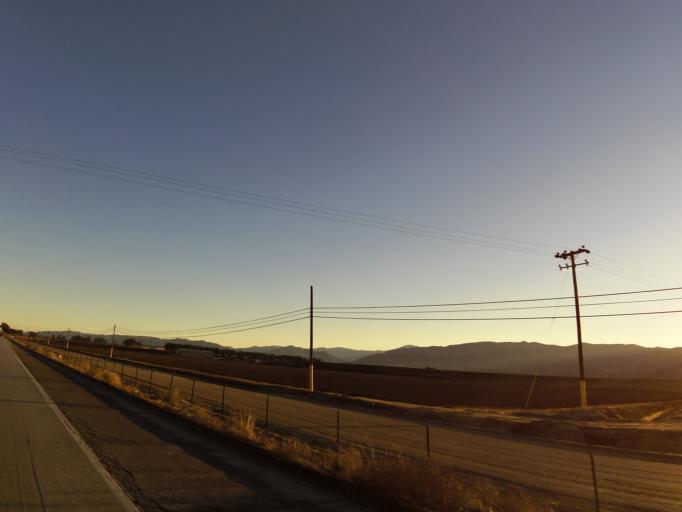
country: US
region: California
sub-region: Monterey County
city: Soledad
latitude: 36.3945
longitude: -121.3106
